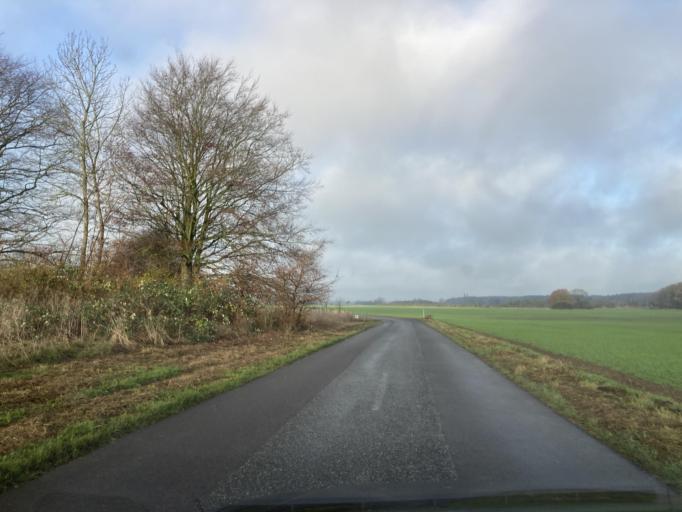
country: DK
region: Zealand
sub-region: Lolland Kommune
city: Rodby
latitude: 54.7955
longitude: 11.3478
